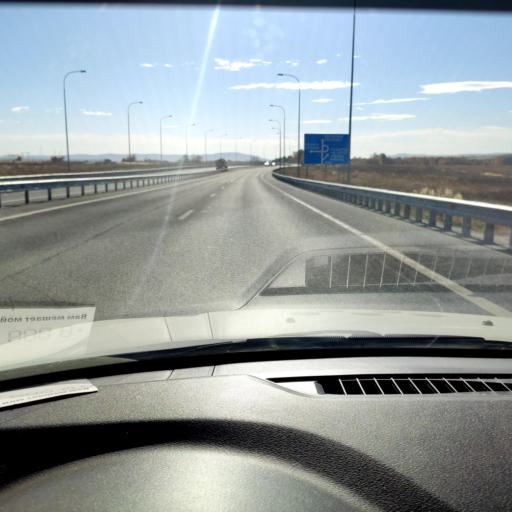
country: RU
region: Samara
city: Bereza
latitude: 53.4970
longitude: 50.1173
